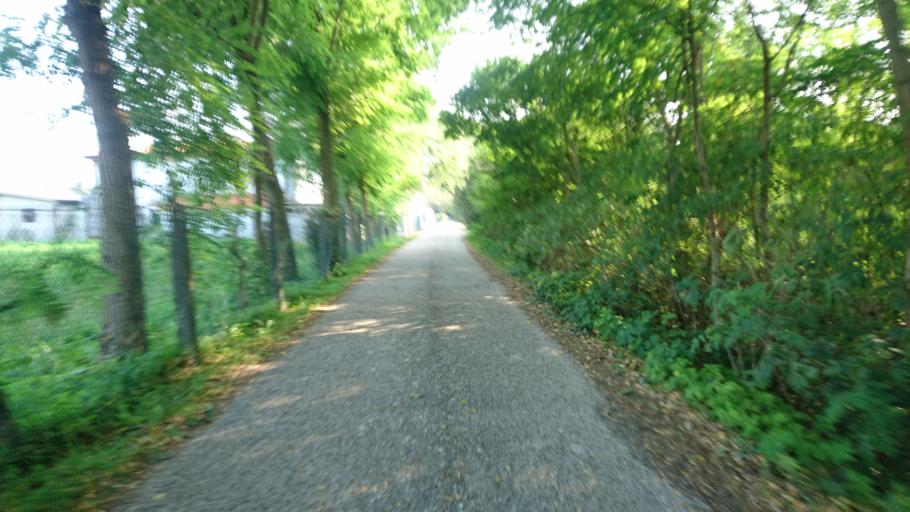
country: IT
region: Veneto
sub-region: Provincia di Padova
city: Pieve
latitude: 45.5413
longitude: 11.8094
